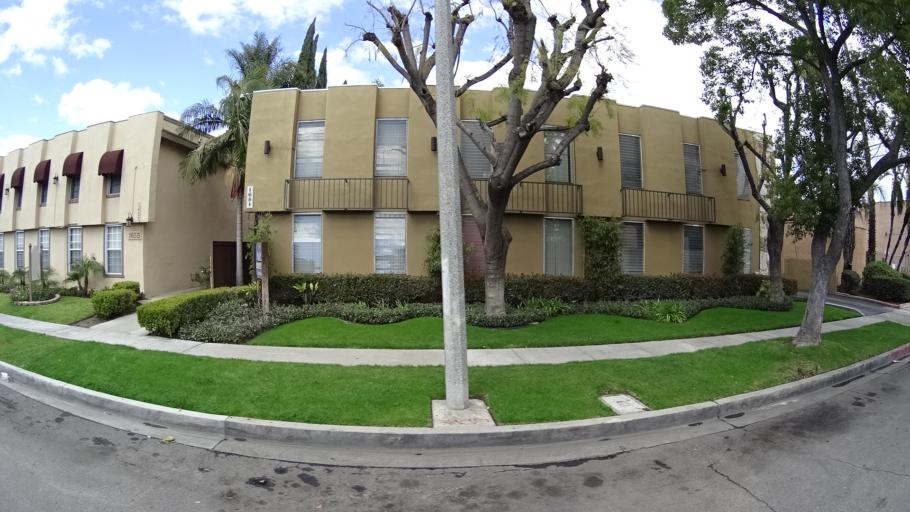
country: US
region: California
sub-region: Orange County
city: Anaheim
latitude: 33.8307
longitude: -117.9395
